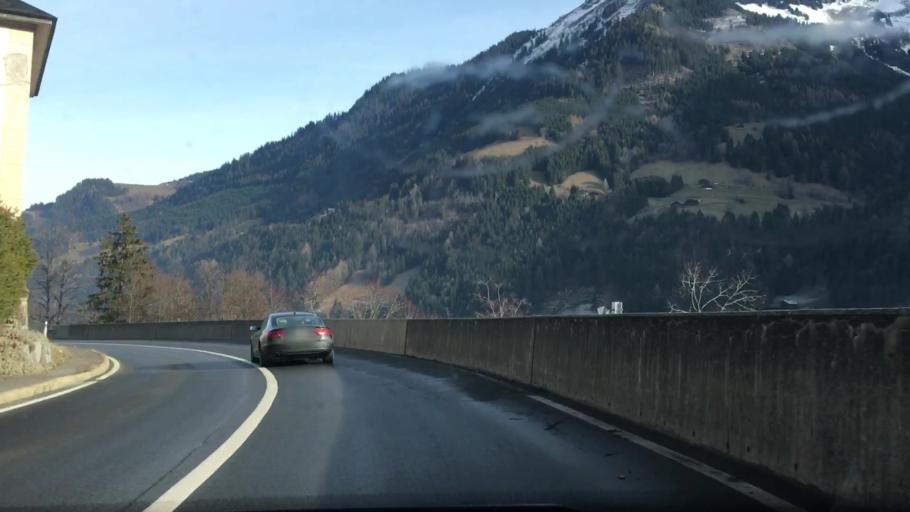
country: CH
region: Valais
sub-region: Monthey District
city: Champery
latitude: 46.1837
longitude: 6.8808
